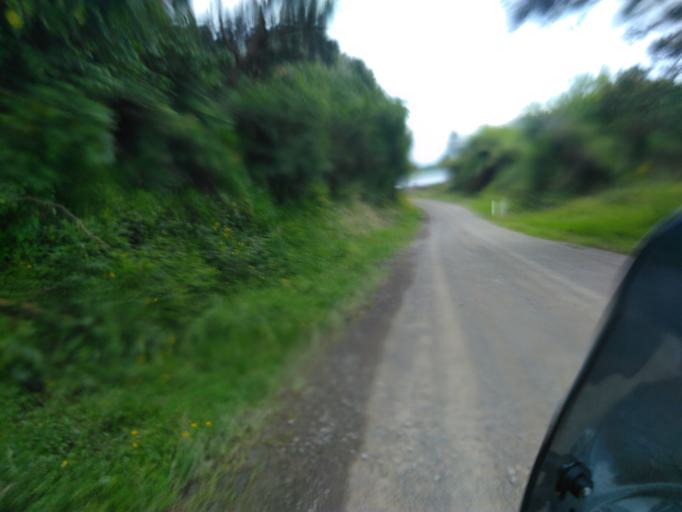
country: NZ
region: Bay of Plenty
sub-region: Opotiki District
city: Opotiki
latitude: -38.0249
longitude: 177.4375
